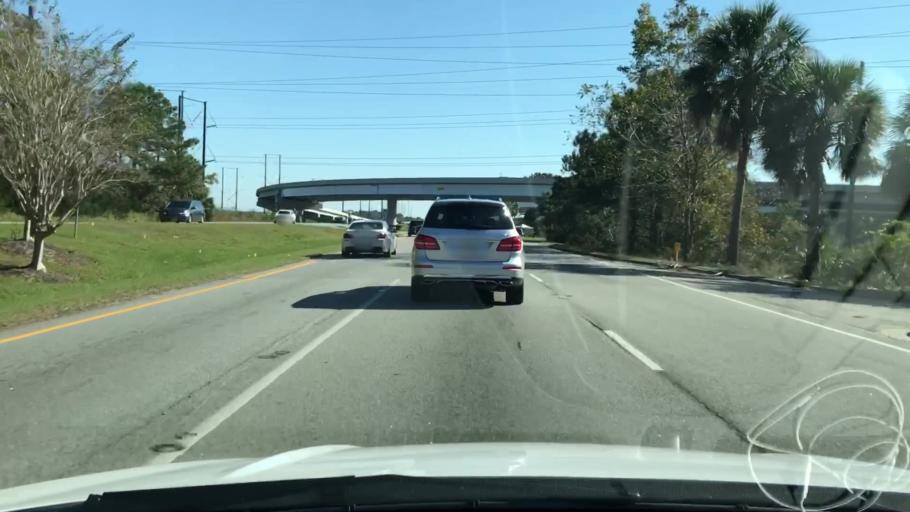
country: US
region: South Carolina
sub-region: Beaufort County
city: Bluffton
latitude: 32.2353
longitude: -80.8051
